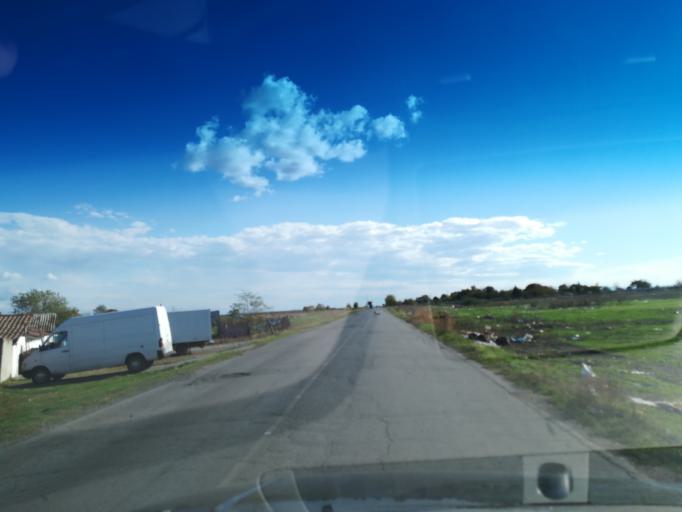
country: BG
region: Stara Zagora
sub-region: Obshtina Chirpan
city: Chirpan
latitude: 42.2014
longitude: 25.3095
